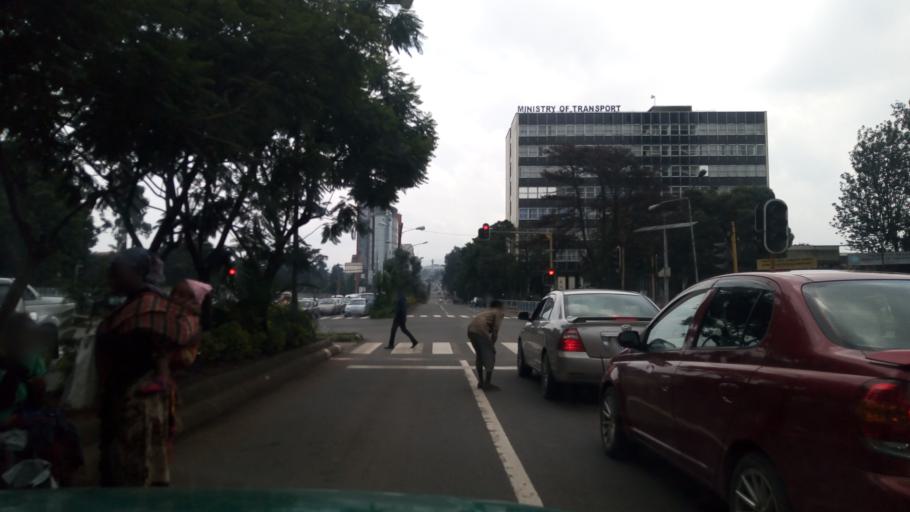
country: ET
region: Adis Abeba
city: Addis Ababa
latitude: 9.0189
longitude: 38.7524
